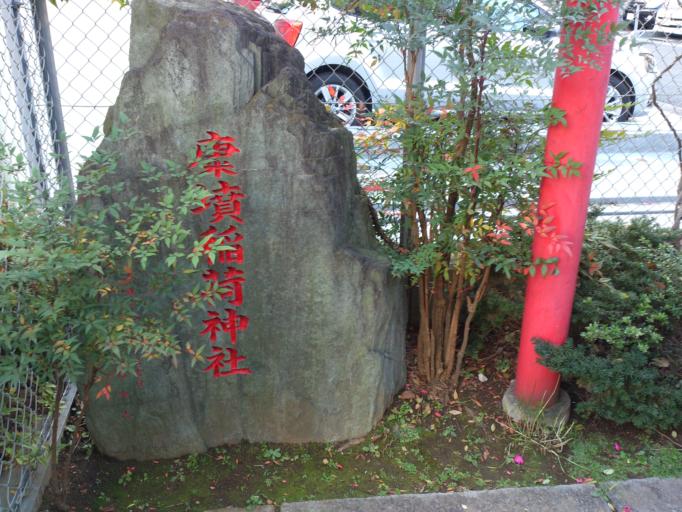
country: JP
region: Chiba
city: Matsudo
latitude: 35.7840
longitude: 139.8982
